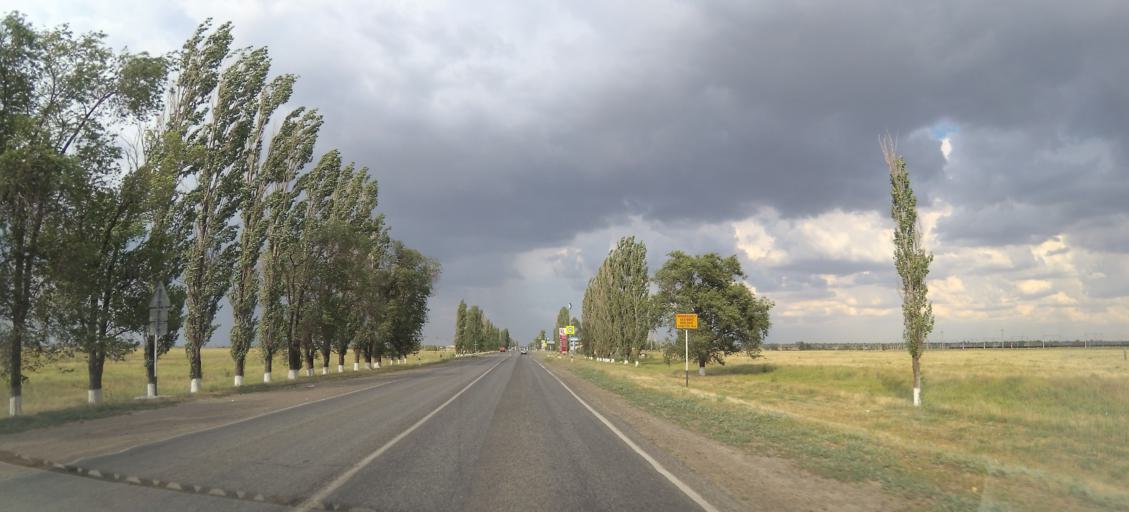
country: RU
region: Rostov
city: Zimovniki
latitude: 47.1386
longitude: 42.4317
